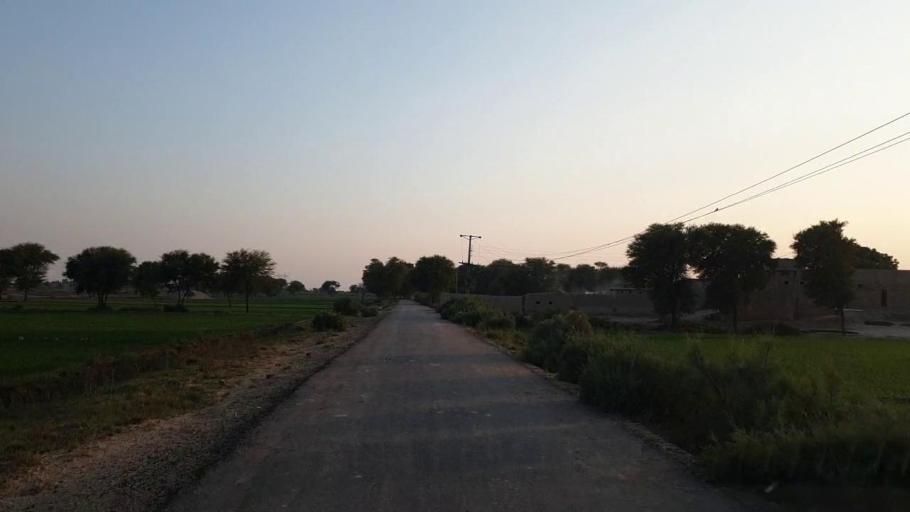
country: PK
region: Sindh
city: Sehwan
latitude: 26.4437
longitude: 67.7618
